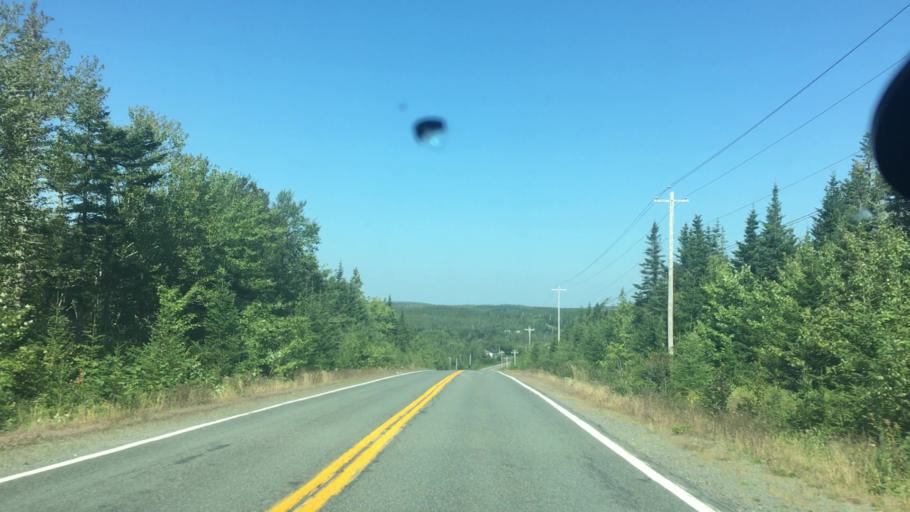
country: CA
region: Nova Scotia
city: Antigonish
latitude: 44.9941
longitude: -62.0979
